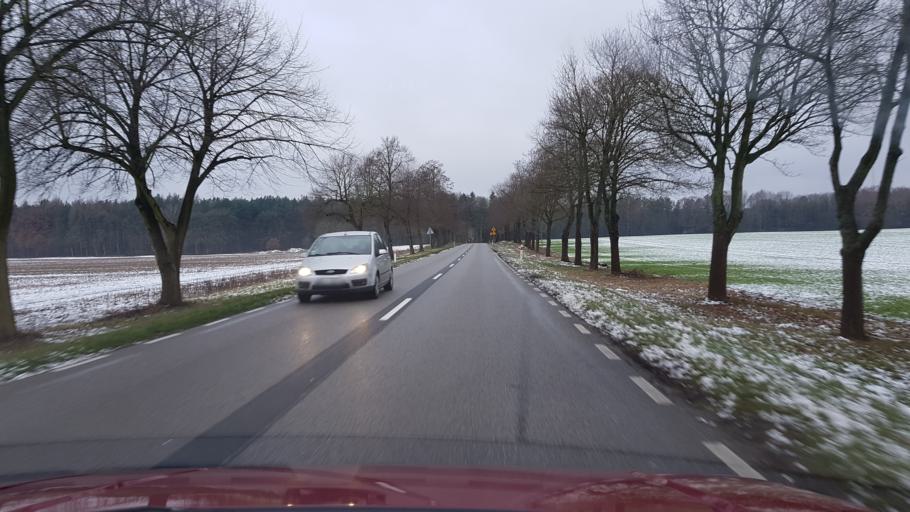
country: PL
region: West Pomeranian Voivodeship
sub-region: Powiat goleniowski
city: Nowogard
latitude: 53.6591
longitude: 15.1757
